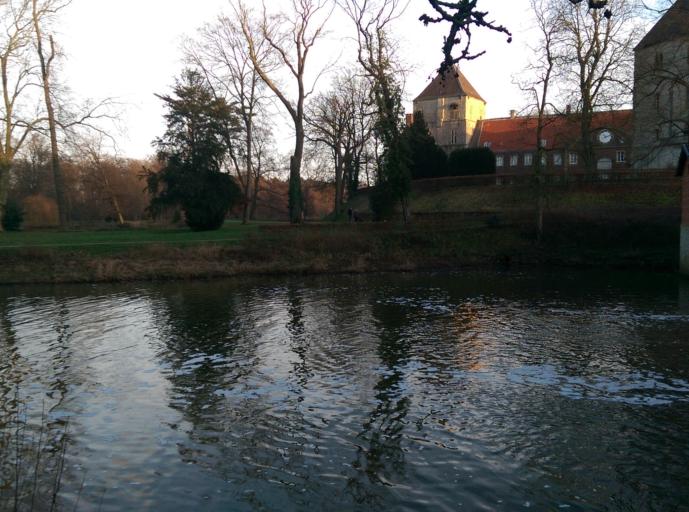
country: DE
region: North Rhine-Westphalia
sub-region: Regierungsbezirk Detmold
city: Rheda-Wiedenbruck
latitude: 51.8516
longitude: 8.2953
